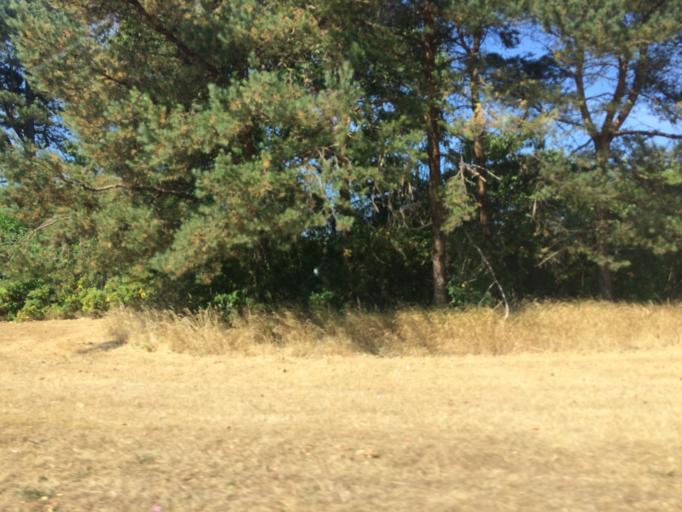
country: DK
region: Central Jutland
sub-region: Holstebro Kommune
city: Holstebro
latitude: 56.3634
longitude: 8.6115
